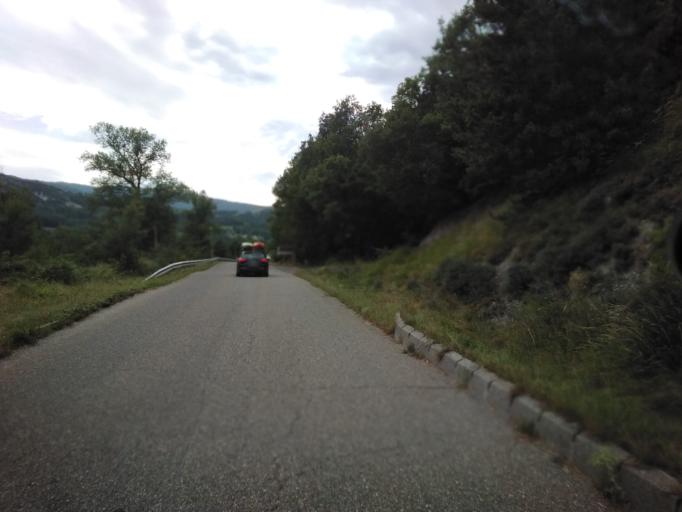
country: FR
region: Provence-Alpes-Cote d'Azur
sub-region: Departement des Alpes-de-Haute-Provence
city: Seyne-les-Alpes
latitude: 44.4639
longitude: 6.3664
